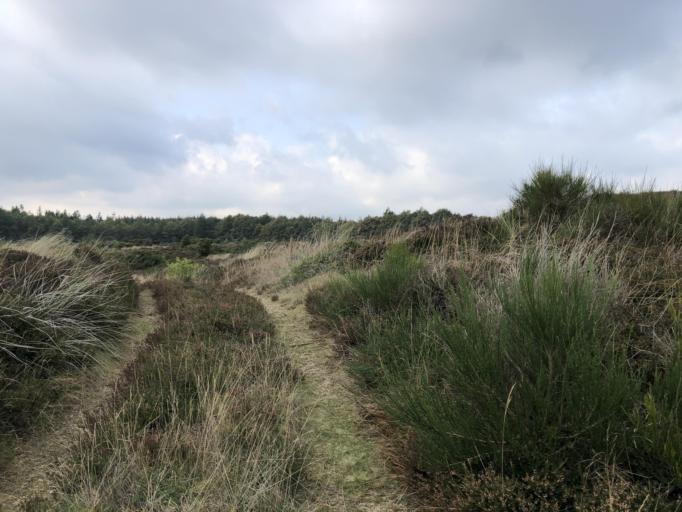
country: DK
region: Central Jutland
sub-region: Holstebro Kommune
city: Ulfborg
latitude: 56.2138
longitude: 8.4285
